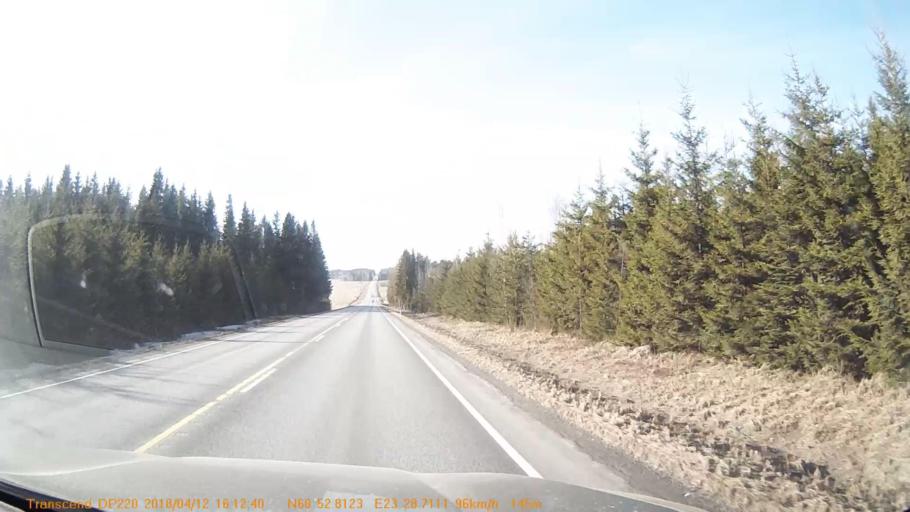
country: FI
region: Haeme
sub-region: Forssa
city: Jokioinen
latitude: 60.8805
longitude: 23.4780
